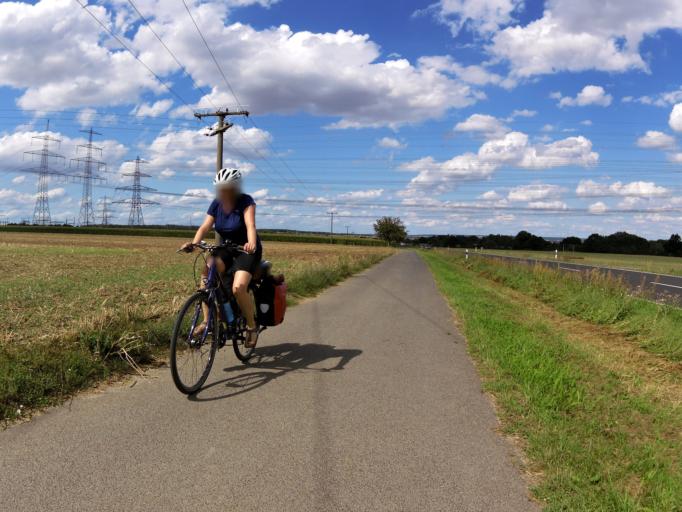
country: DE
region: Bavaria
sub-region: Regierungsbezirk Unterfranken
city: Bergrheinfeld
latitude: 49.9834
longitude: 10.1694
